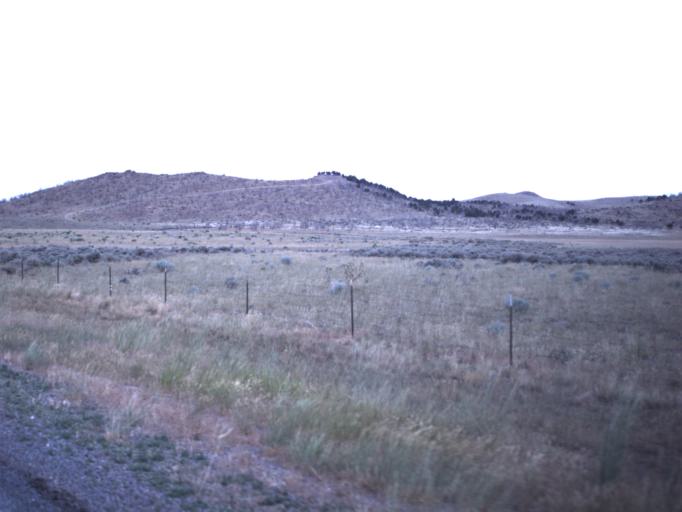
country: US
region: Utah
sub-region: Beaver County
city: Beaver
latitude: 38.6089
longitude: -112.5954
